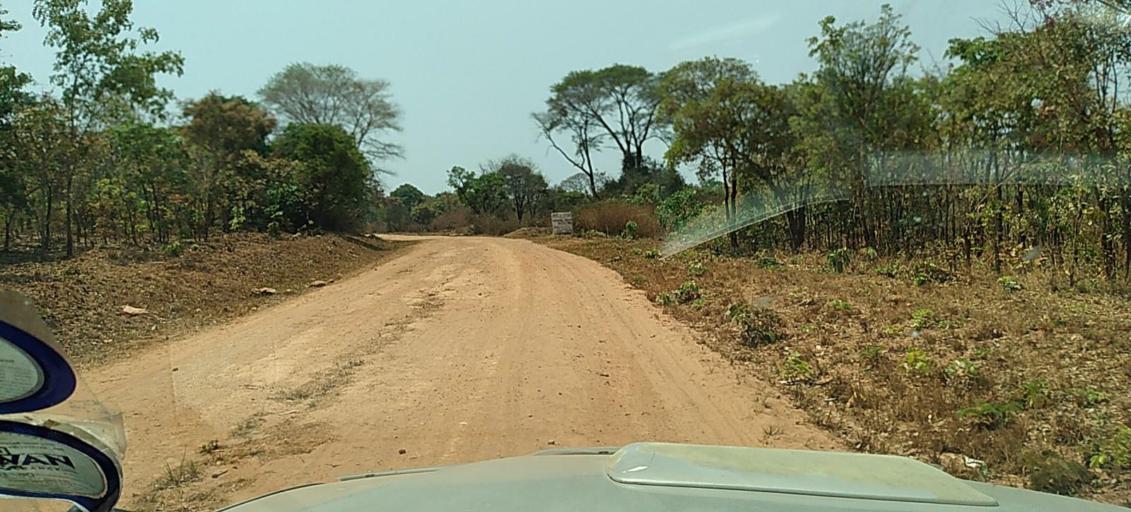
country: ZM
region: North-Western
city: Kasempa
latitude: -13.5509
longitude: 26.0262
